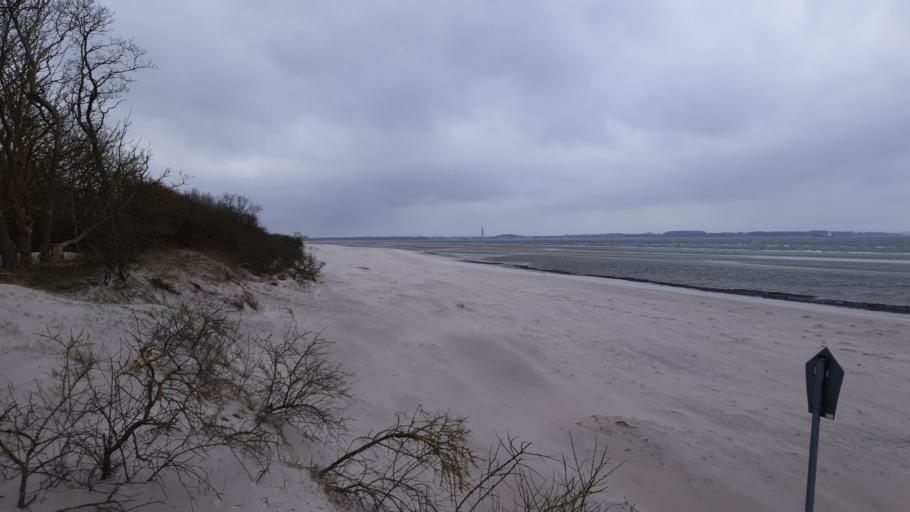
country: DE
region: Mecklenburg-Vorpommern
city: Kalkhorst
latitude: 53.9841
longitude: 10.9742
